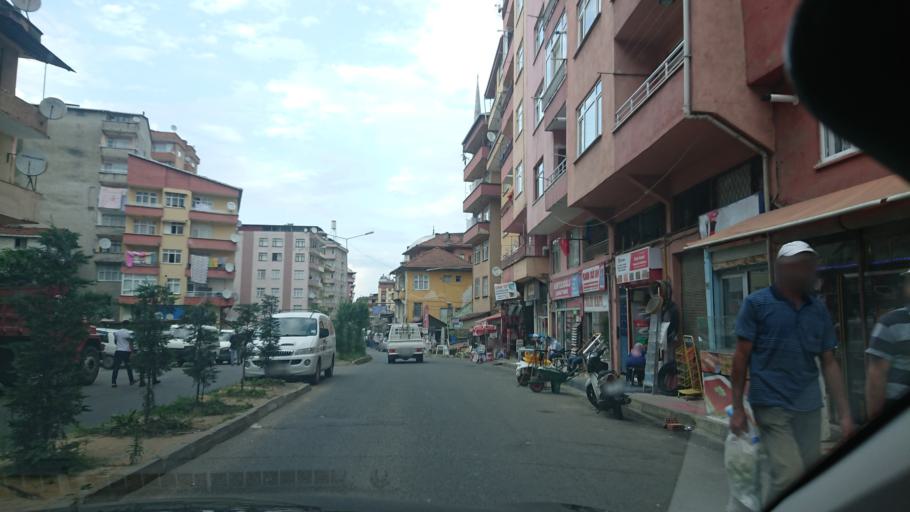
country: TR
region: Rize
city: Rize
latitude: 41.0206
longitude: 40.5179
